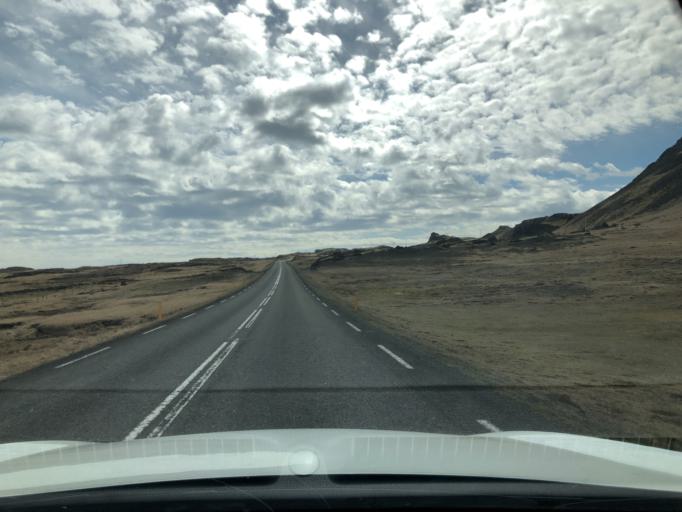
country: IS
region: East
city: Reydarfjoerdur
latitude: 64.6666
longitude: -14.3180
